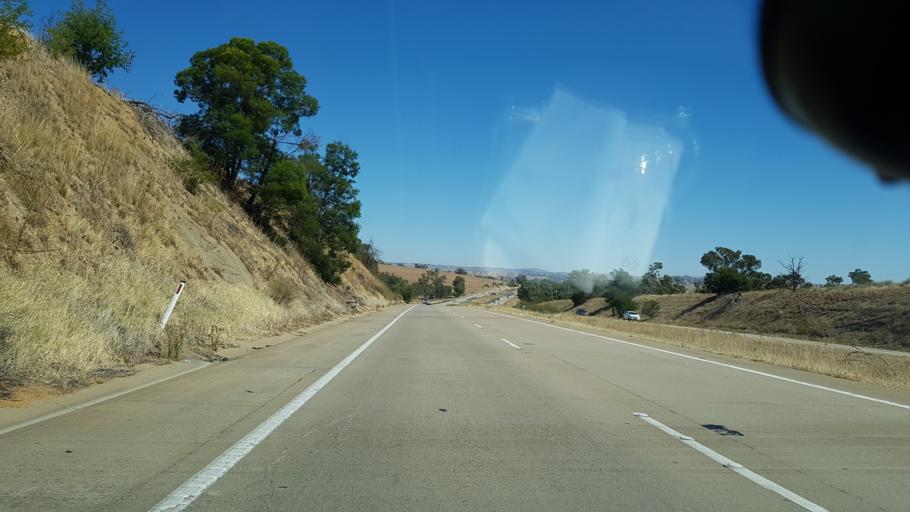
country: AU
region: New South Wales
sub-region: Gundagai
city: Gundagai
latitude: -34.8141
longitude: 148.4116
